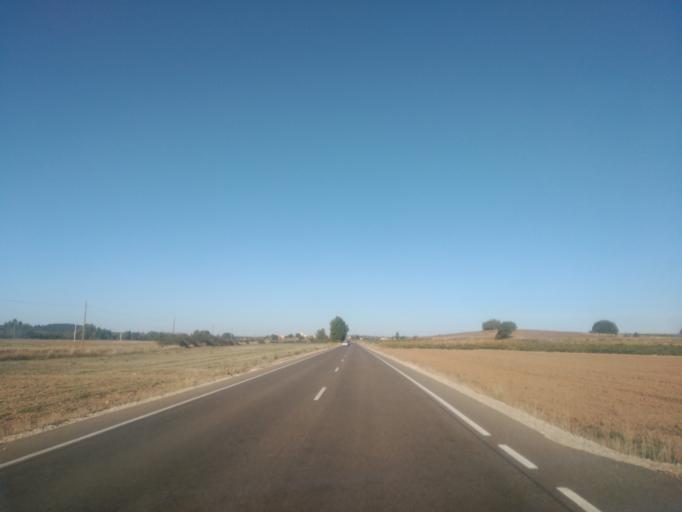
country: ES
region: Castille and Leon
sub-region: Provincia de Burgos
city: San Juan del Monte
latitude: 41.6926
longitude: -3.5325
